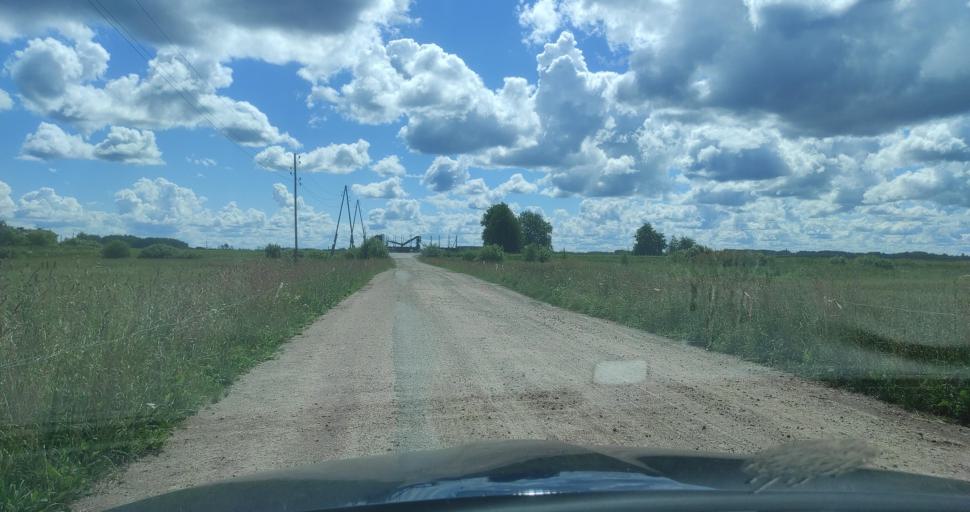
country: LV
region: Kuldigas Rajons
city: Kuldiga
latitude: 57.0014
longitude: 22.1307
